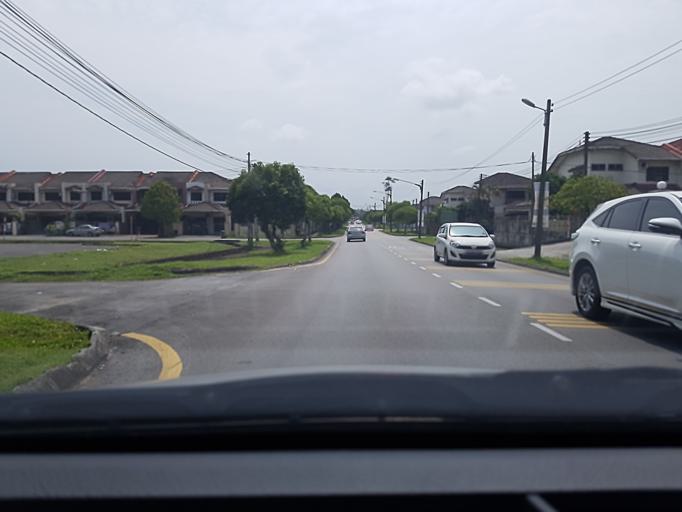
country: MY
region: Sarawak
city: Kuching
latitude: 1.5131
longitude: 110.3619
